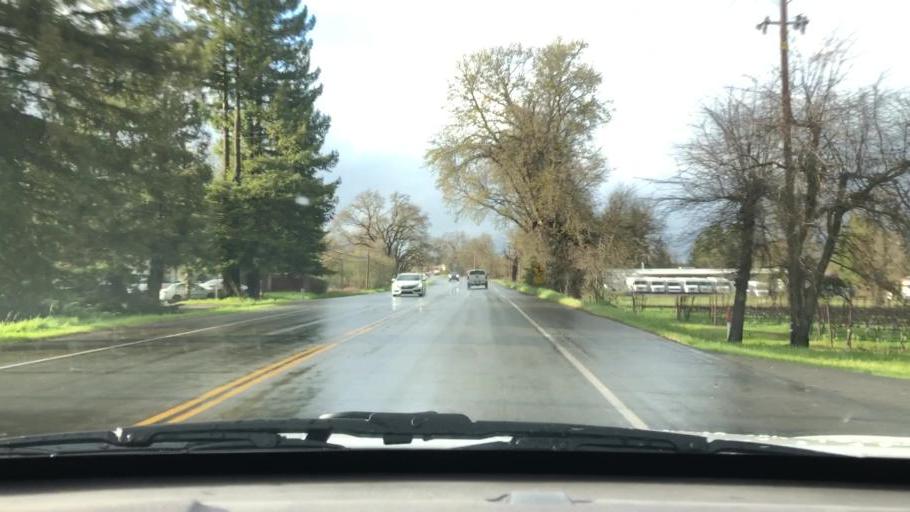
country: US
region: California
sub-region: Mendocino County
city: Ukiah
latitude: 39.1154
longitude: -123.1993
